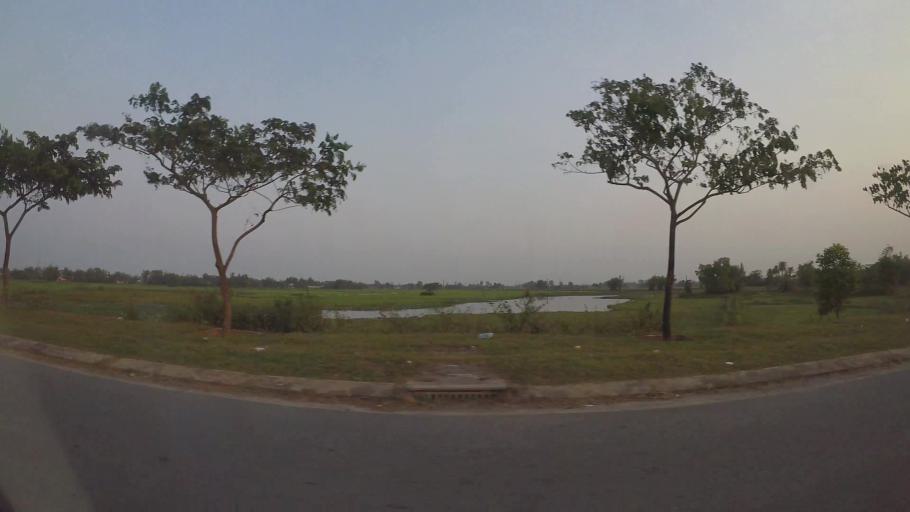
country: VN
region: Da Nang
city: Cam Le
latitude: 15.9721
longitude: 108.2241
